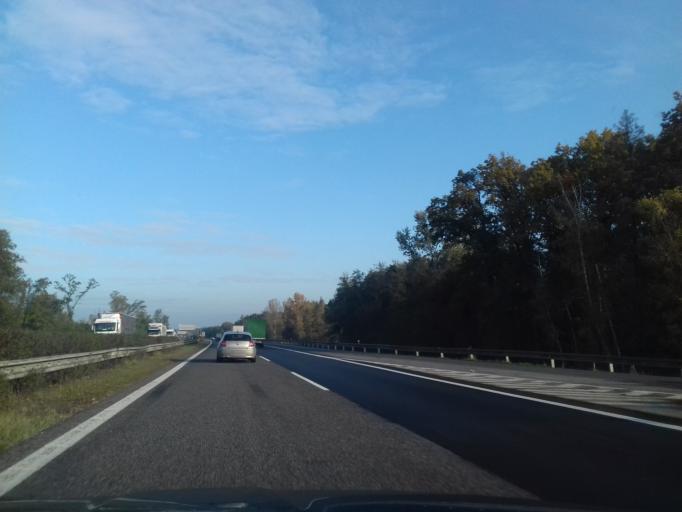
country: SK
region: Bratislavsky
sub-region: Okres Malacky
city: Malacky
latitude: 48.4297
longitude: 17.0426
